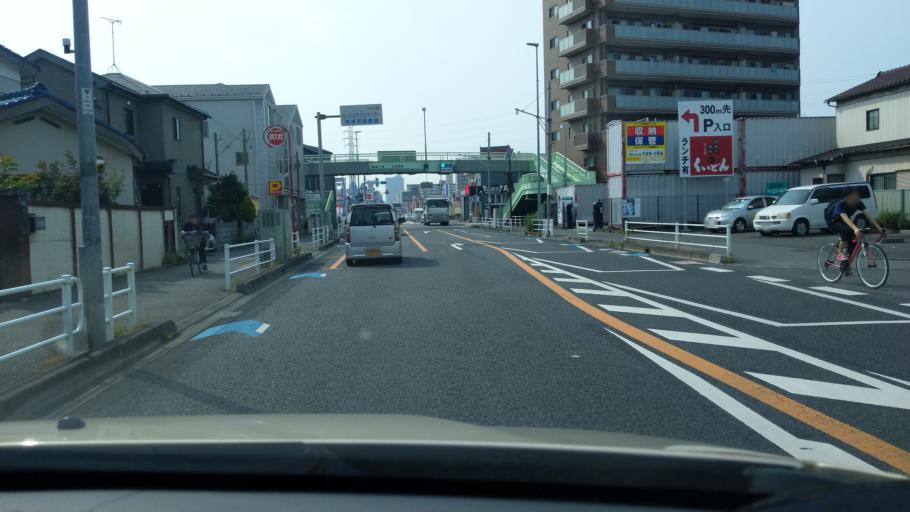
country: JP
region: Saitama
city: Shimotoda
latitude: 35.8366
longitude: 139.6646
